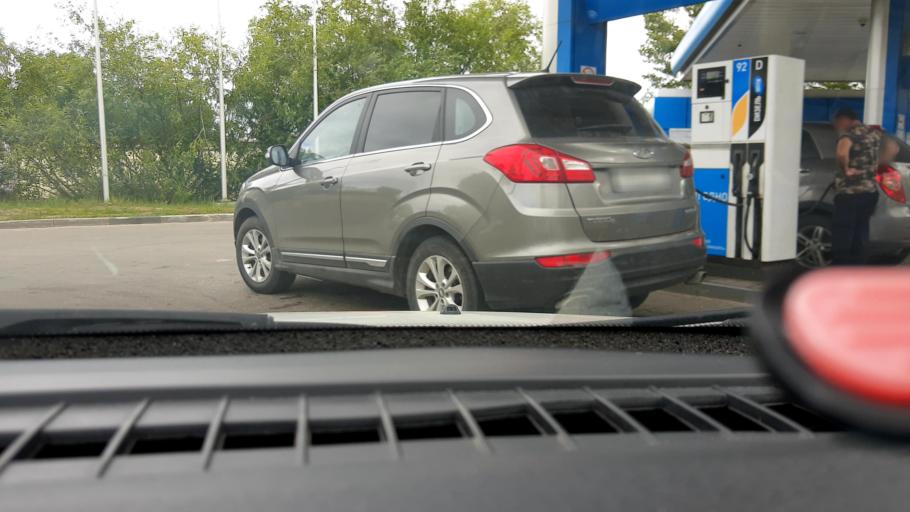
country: RU
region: Nizjnij Novgorod
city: Dzerzhinsk
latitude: 56.2427
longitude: 43.5078
